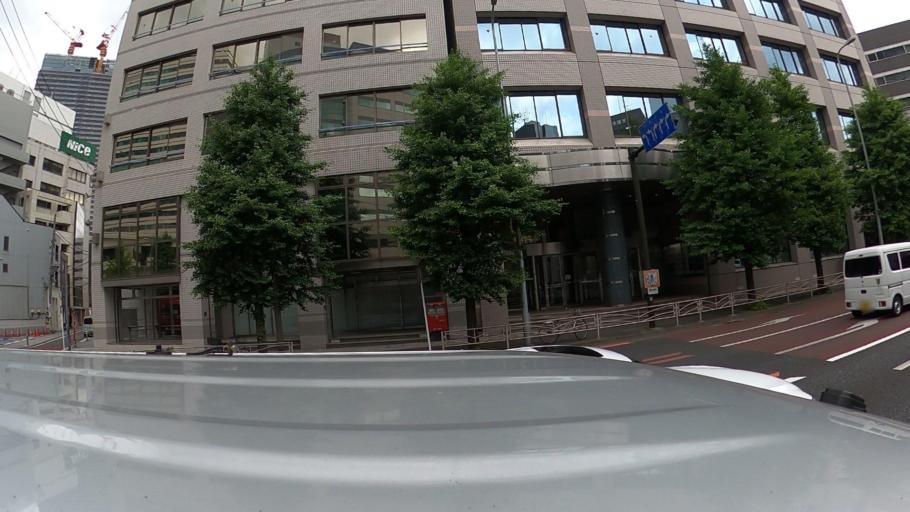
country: JP
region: Kanagawa
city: Yokohama
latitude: 35.4694
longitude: 139.6268
